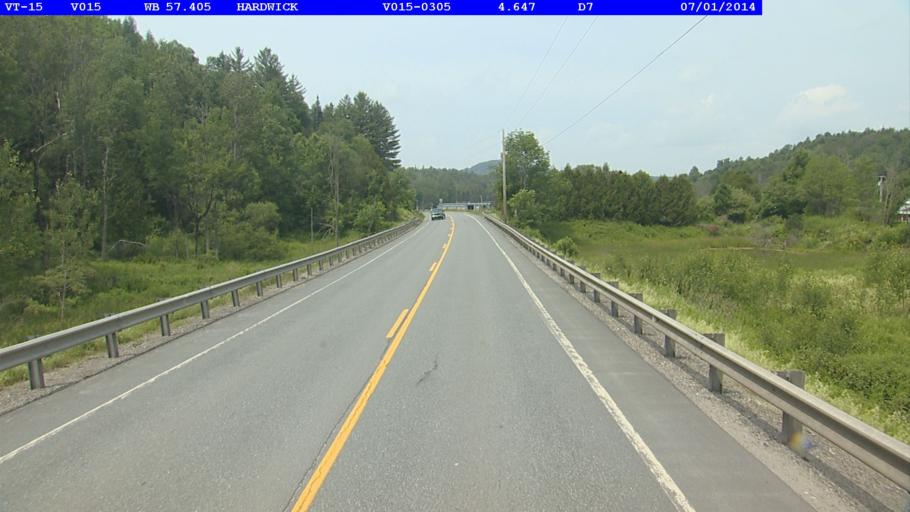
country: US
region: Vermont
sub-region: Caledonia County
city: Hardwick
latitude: 44.5025
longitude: -72.3440
